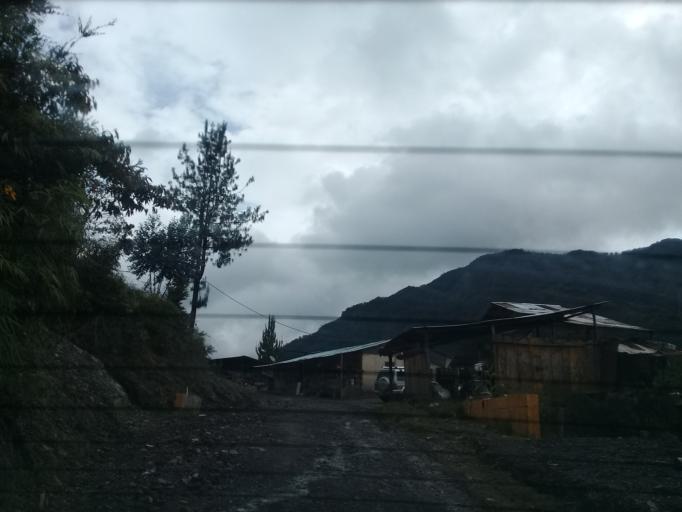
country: CO
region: Cundinamarca
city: Gachala
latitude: 4.7017
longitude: -73.4447
